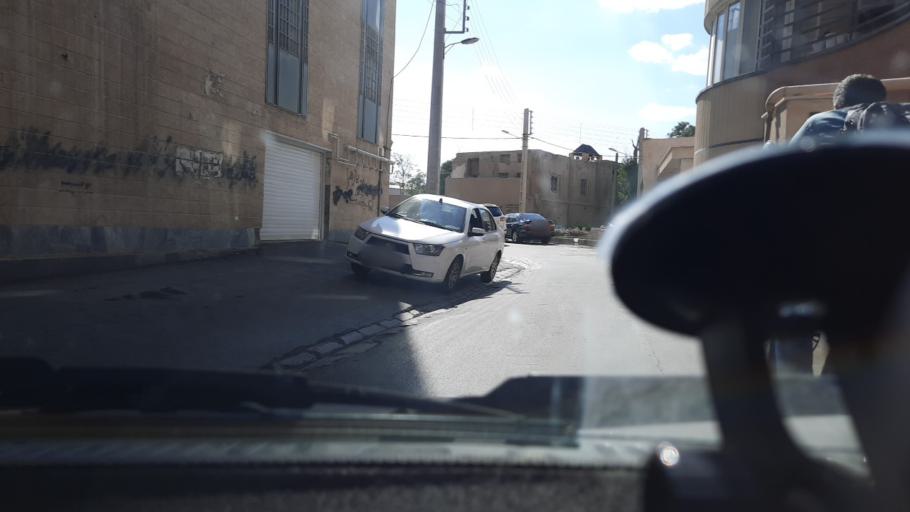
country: IR
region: Markazi
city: Arak
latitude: 34.0819
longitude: 49.6903
